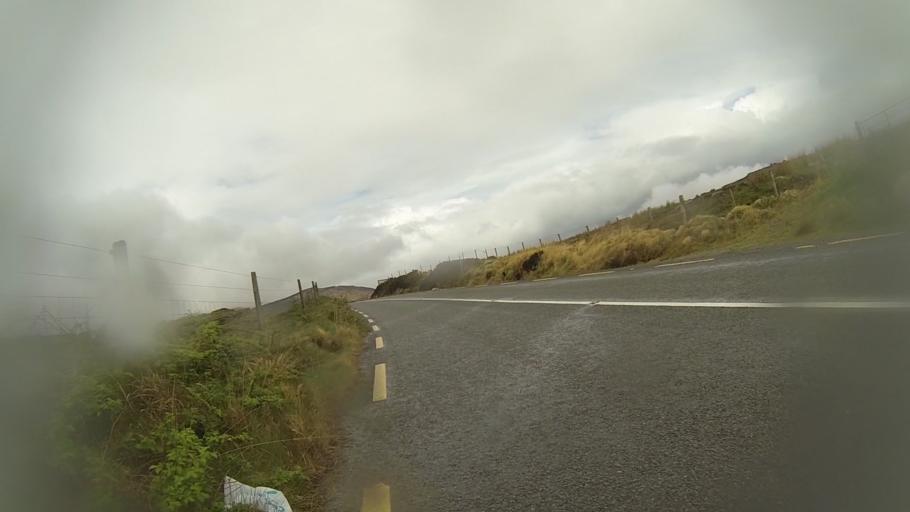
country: IE
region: Munster
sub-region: Ciarrai
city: Kenmare
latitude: 51.8009
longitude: -9.5718
